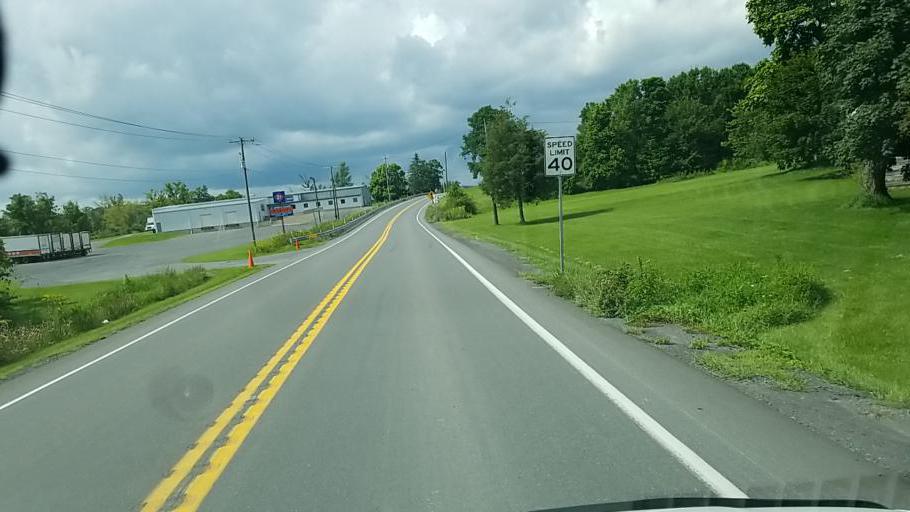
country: US
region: Pennsylvania
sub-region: Dauphin County
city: Elizabethville
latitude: 40.6606
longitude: -76.8278
